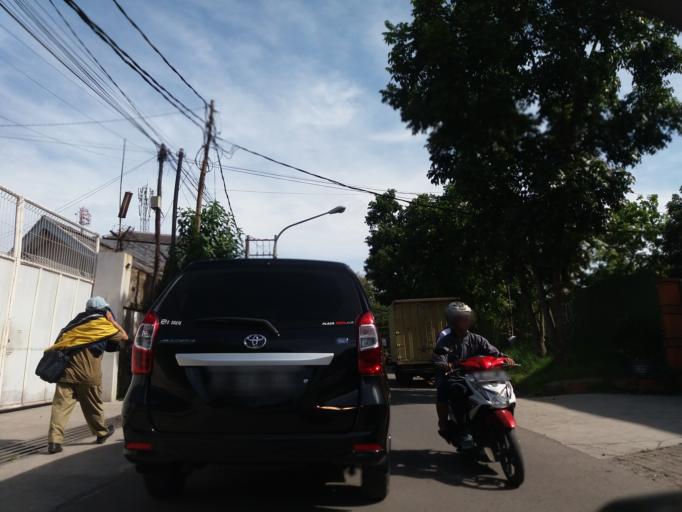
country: ID
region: West Java
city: Bandung
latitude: -6.9406
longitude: 107.6037
